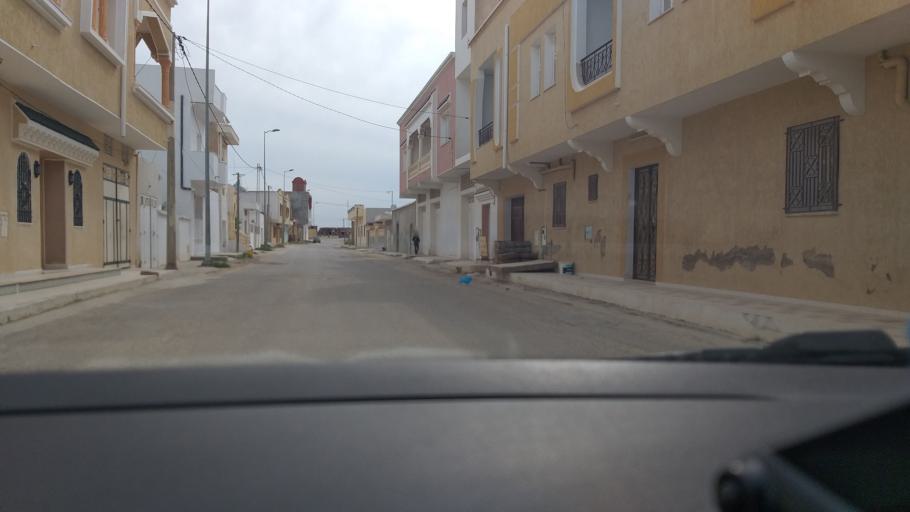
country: TN
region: Al Mahdiyah
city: El Jem
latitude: 35.2852
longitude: 10.7112
